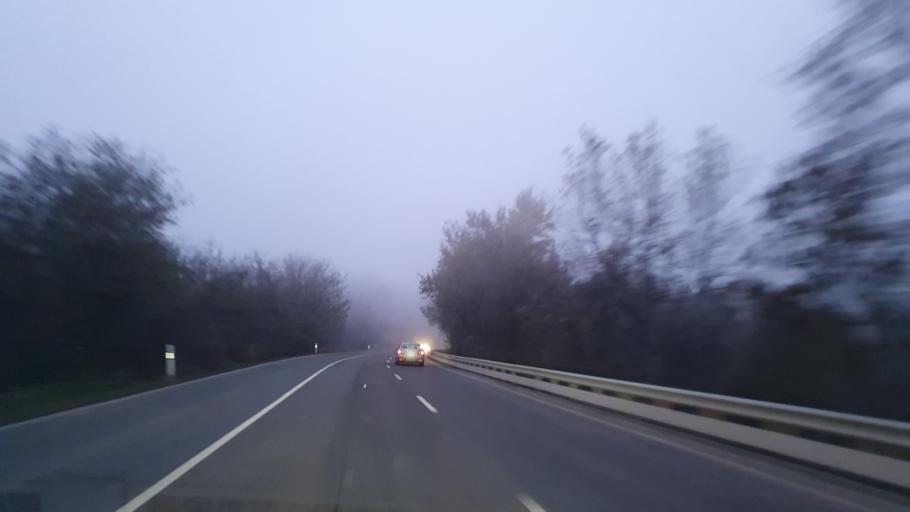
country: HU
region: Pest
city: Kerepes
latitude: 47.5776
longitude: 19.2915
